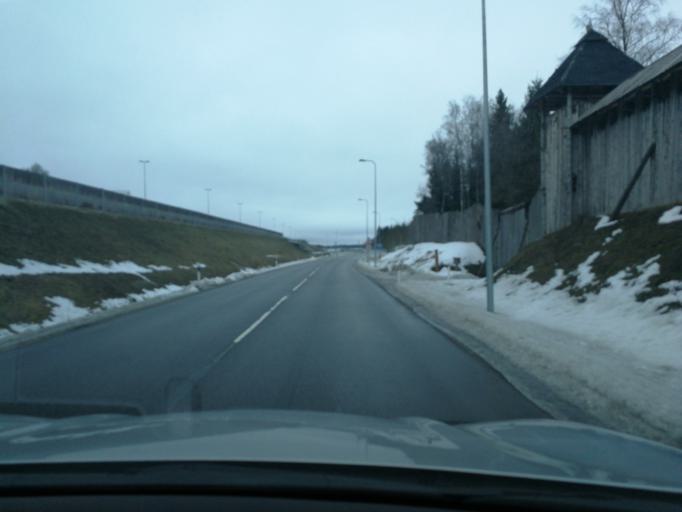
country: EE
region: Harju
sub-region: Rae vald
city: Vaida
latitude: 59.2226
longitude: 25.0336
